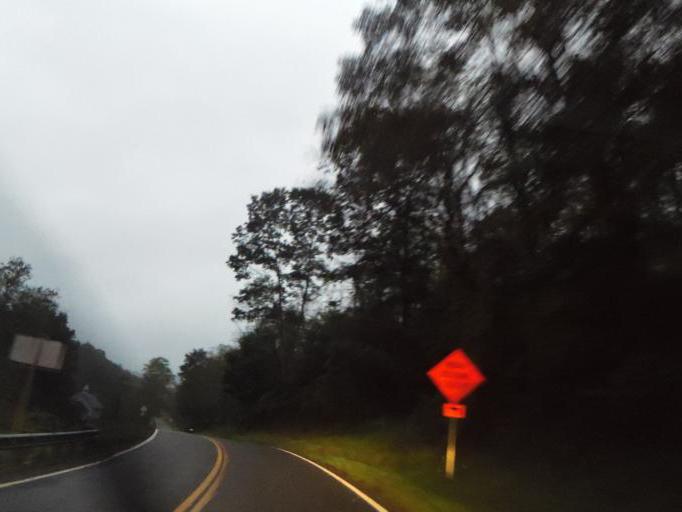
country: US
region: Virginia
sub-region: Grayson County
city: Independence
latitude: 36.5927
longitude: -81.1576
